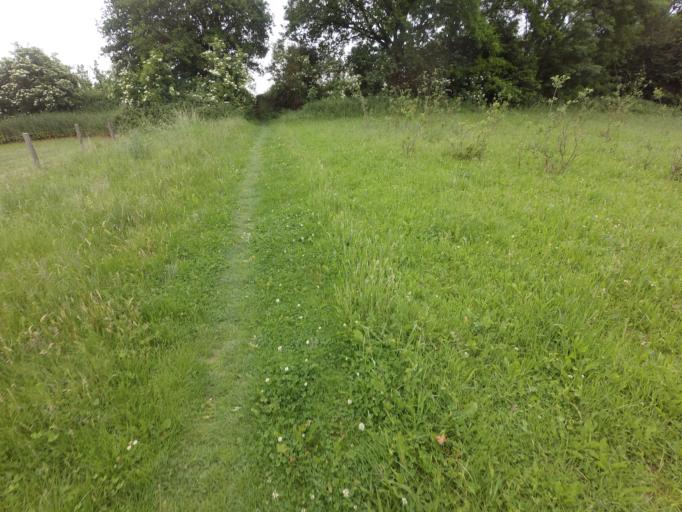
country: NL
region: Limburg
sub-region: Gemeente Voerendaal
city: Ubachsberg
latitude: 50.8656
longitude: 5.9616
